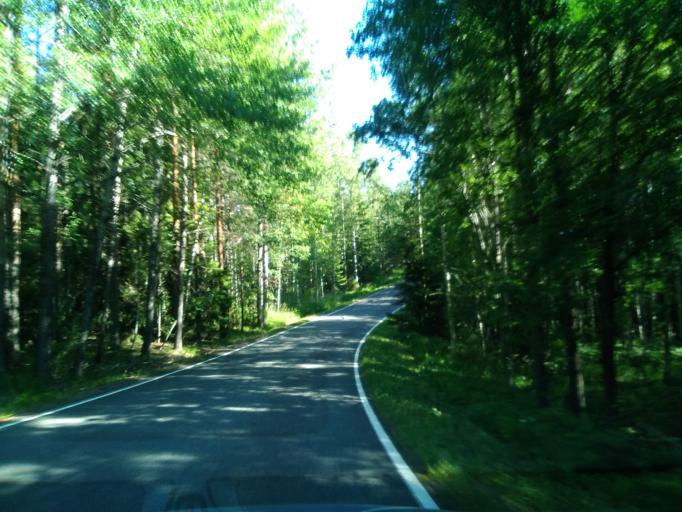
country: FI
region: Uusimaa
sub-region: Helsinki
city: Kaerkoelae
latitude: 60.7818
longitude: 24.0754
